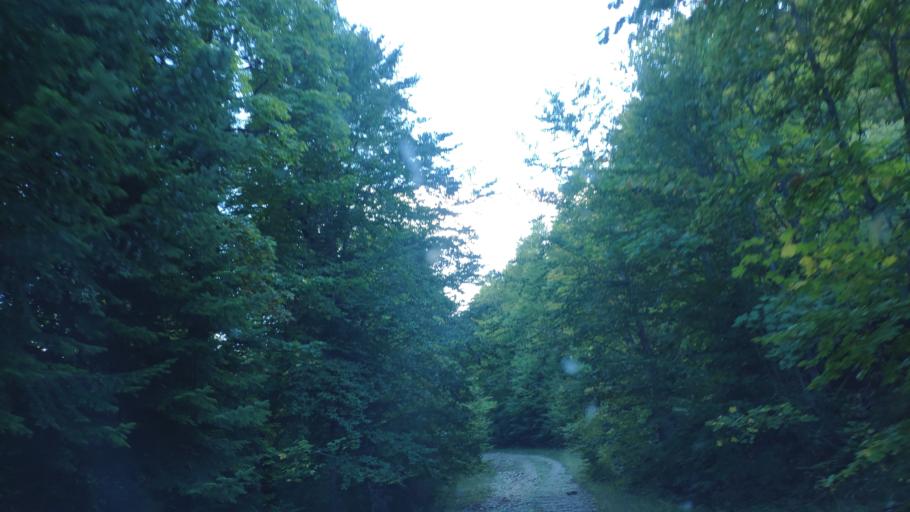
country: AL
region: Korce
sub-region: Rrethi i Devollit
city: Miras
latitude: 40.3589
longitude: 20.8965
